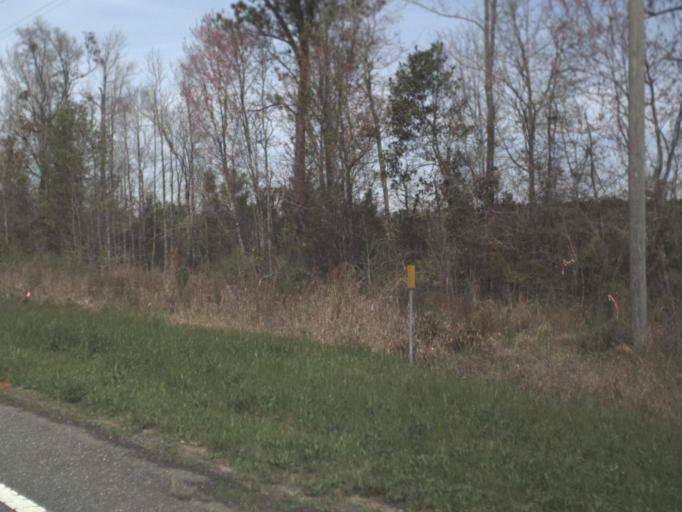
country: US
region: Alabama
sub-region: Geneva County
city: Geneva
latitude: 30.9469
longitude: -85.9788
